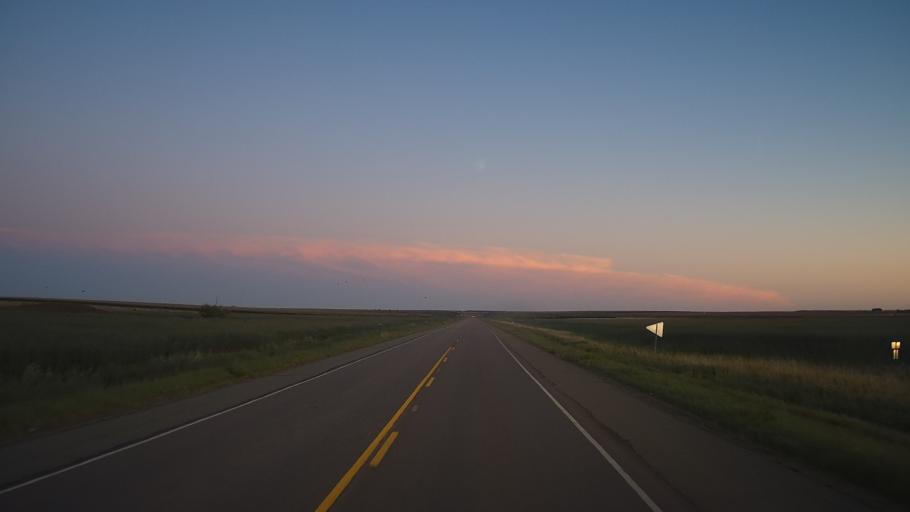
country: US
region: South Dakota
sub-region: Buffalo County
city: Fort Thompson
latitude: 43.8732
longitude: -99.6057
